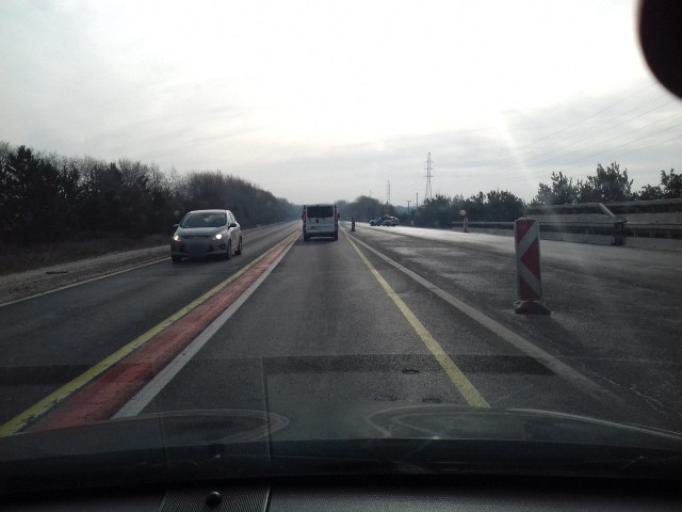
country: HU
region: Pest
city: Fot
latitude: 47.6271
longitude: 19.1672
